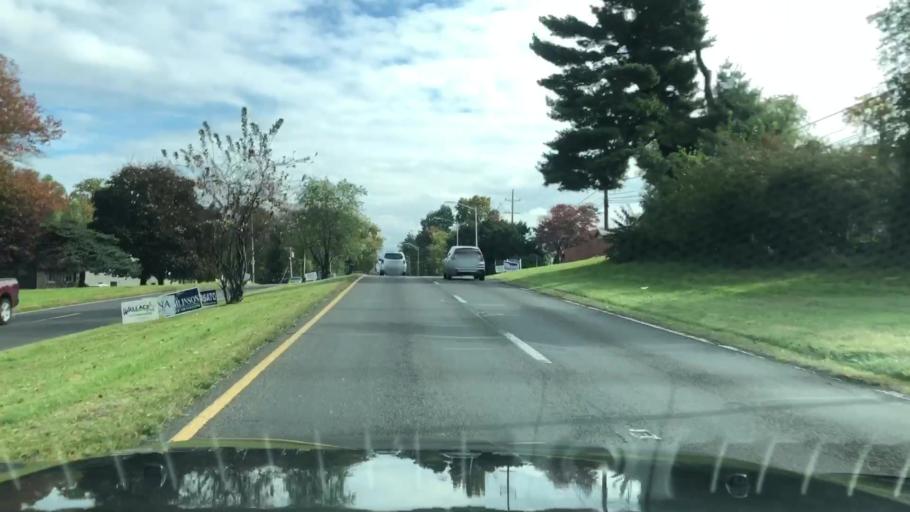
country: US
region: Pennsylvania
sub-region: Bucks County
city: Levittown
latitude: 40.1648
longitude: -74.8401
